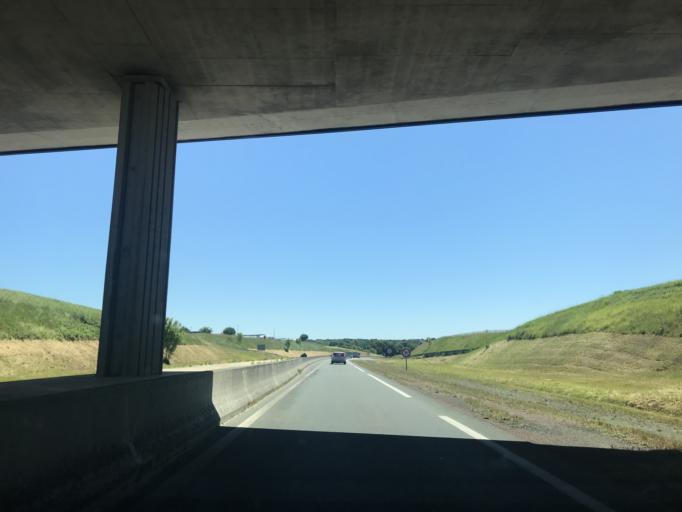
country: FR
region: Poitou-Charentes
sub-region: Departement de la Charente-Maritime
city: Saint-Georges-de-Didonne
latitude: 45.6053
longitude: -0.9743
